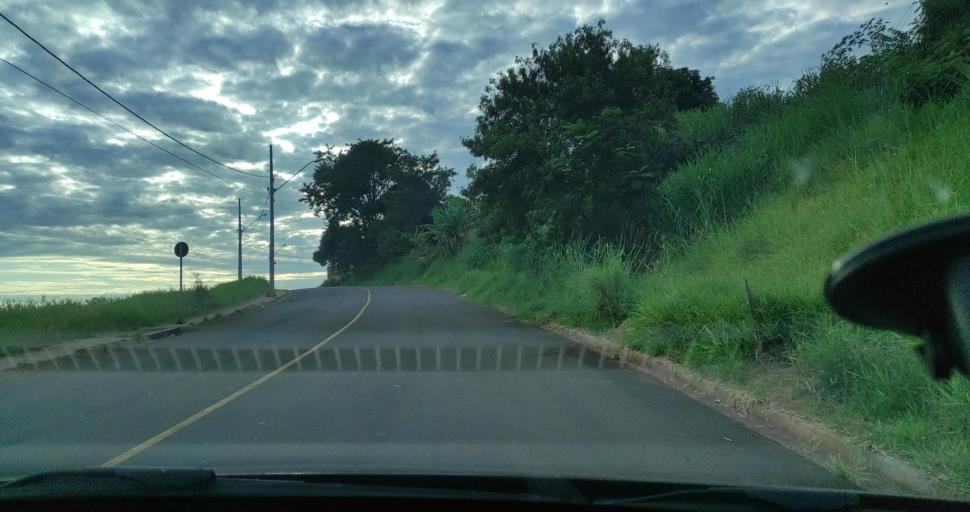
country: BR
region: Parana
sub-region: Ibipora
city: Ibipora
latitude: -23.2636
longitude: -51.0461
